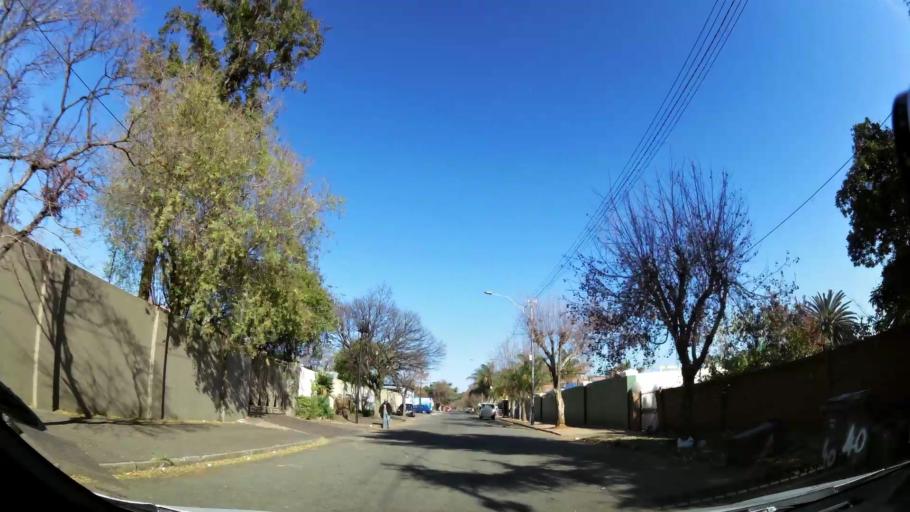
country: ZA
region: Gauteng
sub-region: City of Johannesburg Metropolitan Municipality
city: Johannesburg
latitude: -26.1865
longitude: 28.1079
